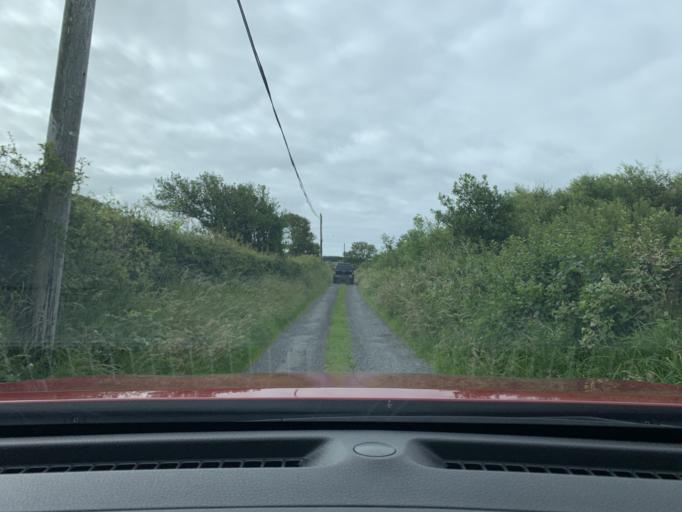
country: IE
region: Connaught
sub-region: Sligo
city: Sligo
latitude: 54.3787
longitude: -8.5210
